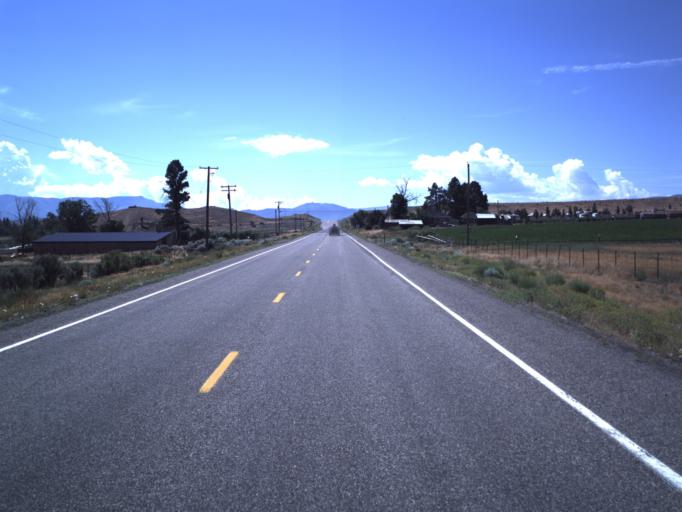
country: US
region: Utah
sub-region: Sevier County
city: Monroe
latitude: 38.4689
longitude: -112.2355
